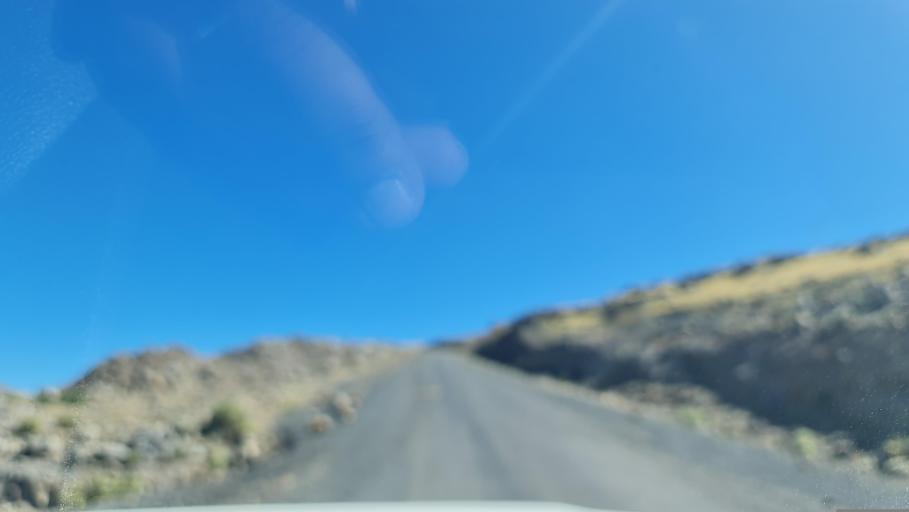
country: ET
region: Amhara
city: Debark'
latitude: 13.1579
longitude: 38.1887
